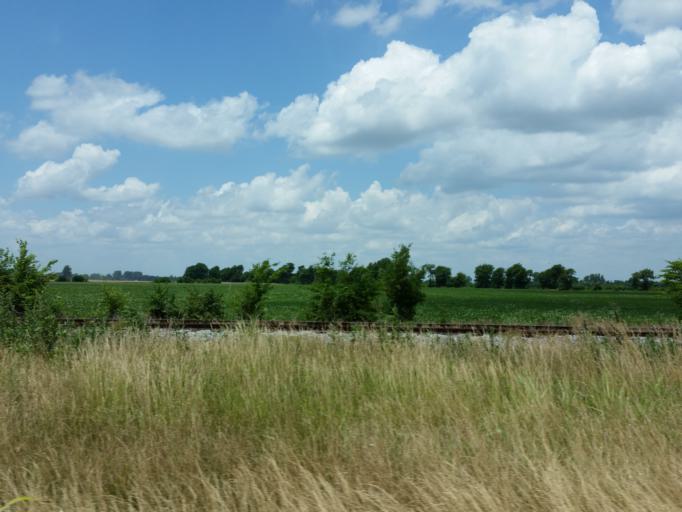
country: US
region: Tennessee
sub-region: Lake County
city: Tiptonville
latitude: 36.3976
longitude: -89.4569
